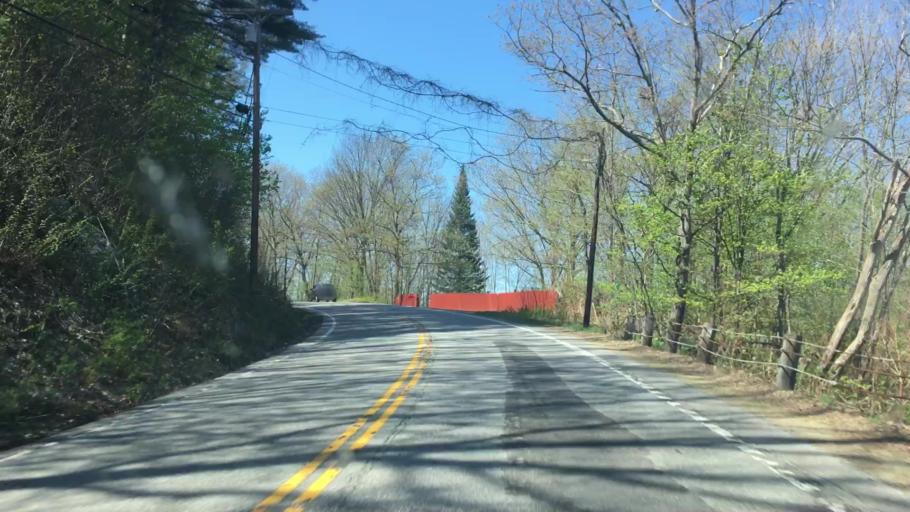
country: US
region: New Hampshire
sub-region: Grafton County
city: Plymouth
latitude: 43.7452
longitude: -71.6804
